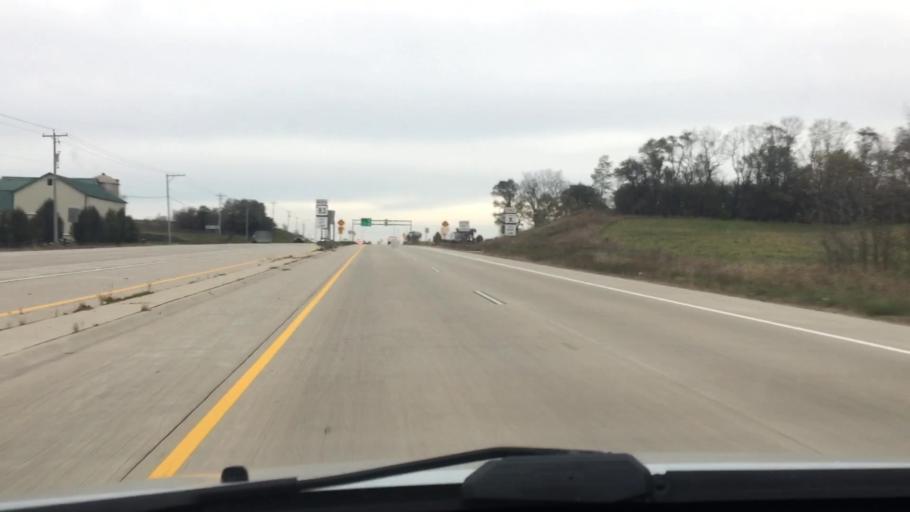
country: US
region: Wisconsin
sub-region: Waukesha County
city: North Prairie
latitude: 42.9308
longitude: -88.3464
